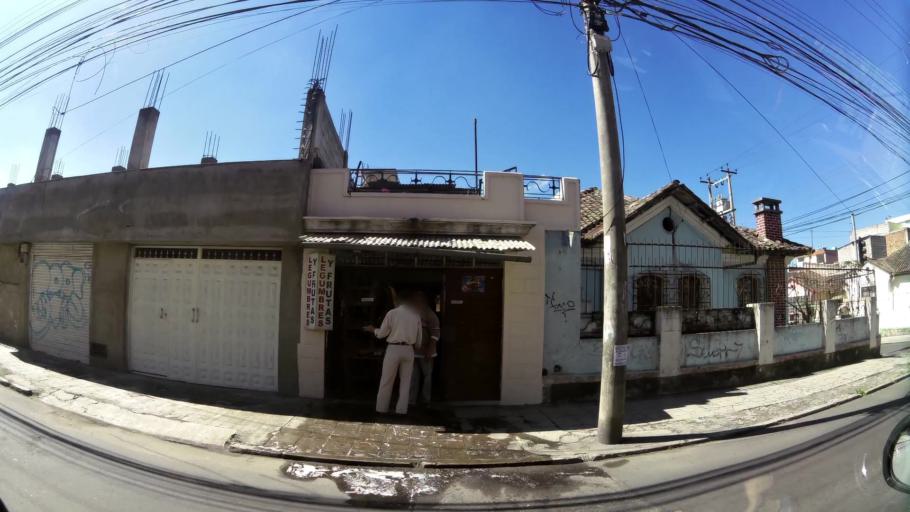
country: EC
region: Pichincha
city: Quito
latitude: -0.2442
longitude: -78.5278
